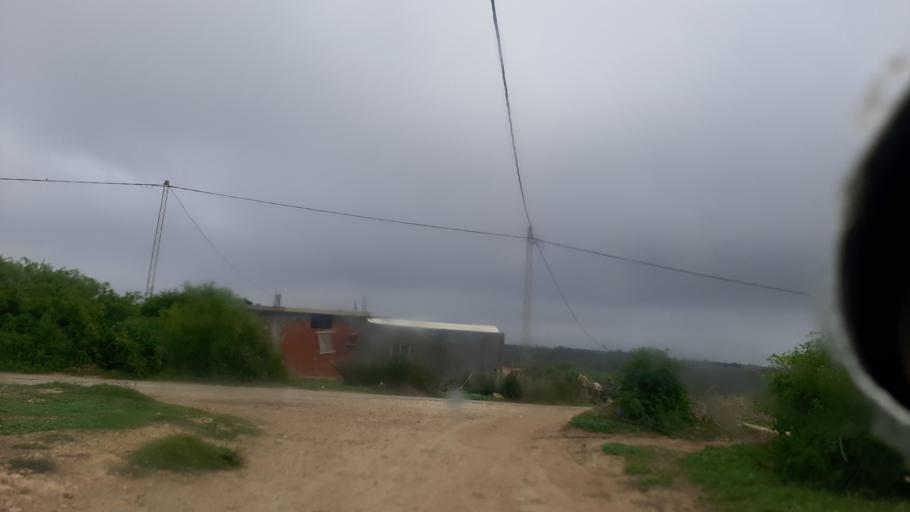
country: TN
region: Nabul
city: Qulaybiyah
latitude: 36.8326
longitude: 11.0378
